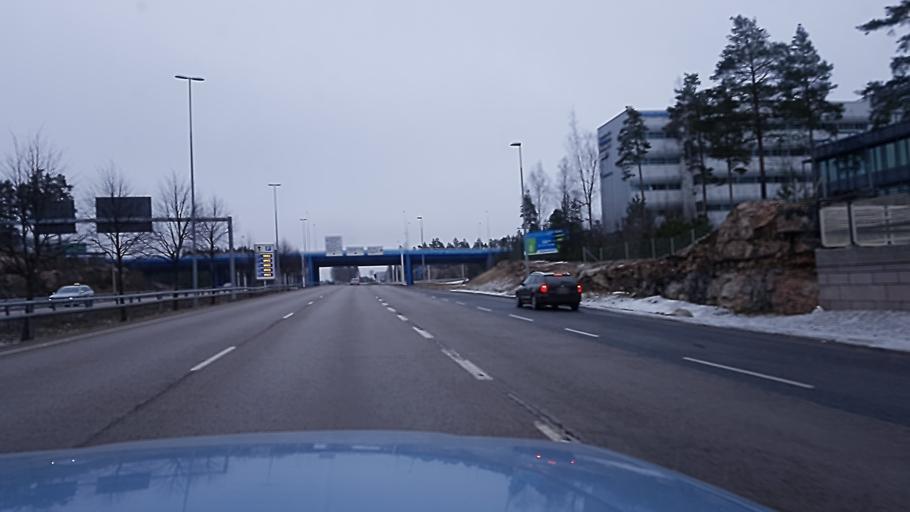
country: FI
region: Uusimaa
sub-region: Helsinki
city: Vantaa
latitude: 60.3053
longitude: 24.9640
